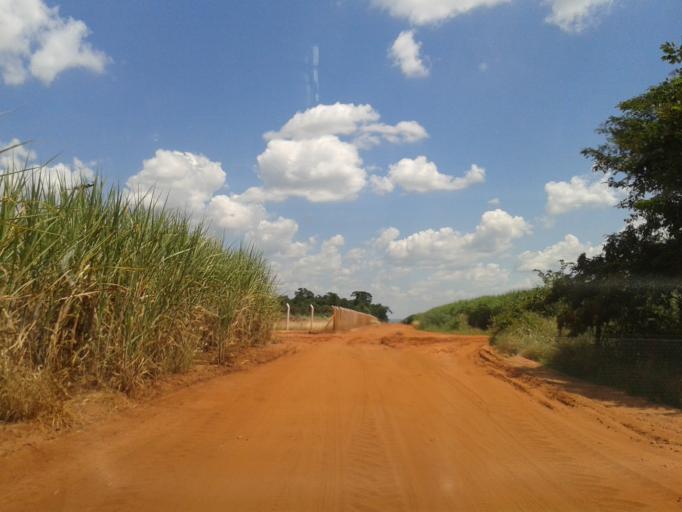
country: BR
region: Minas Gerais
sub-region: Ituiutaba
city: Ituiutaba
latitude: -19.0098
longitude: -49.6772
